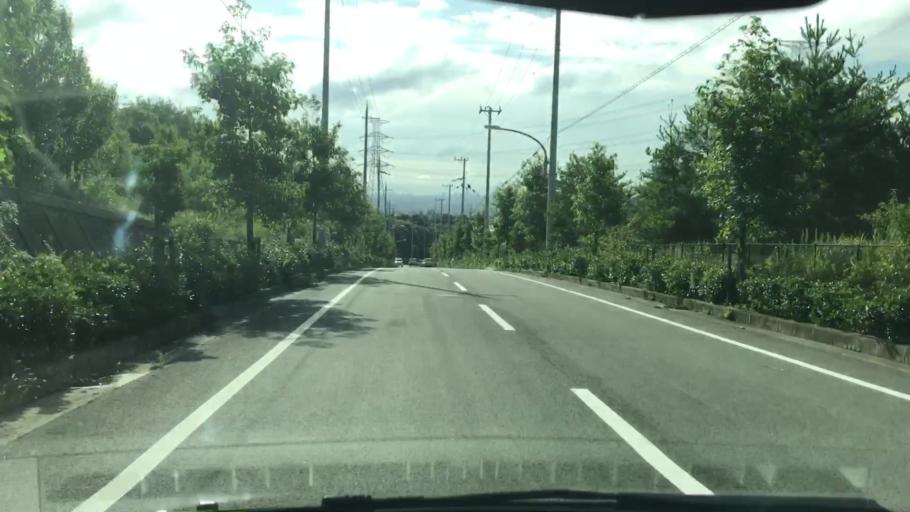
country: JP
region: Hyogo
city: Takarazuka
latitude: 34.8369
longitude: 135.2994
